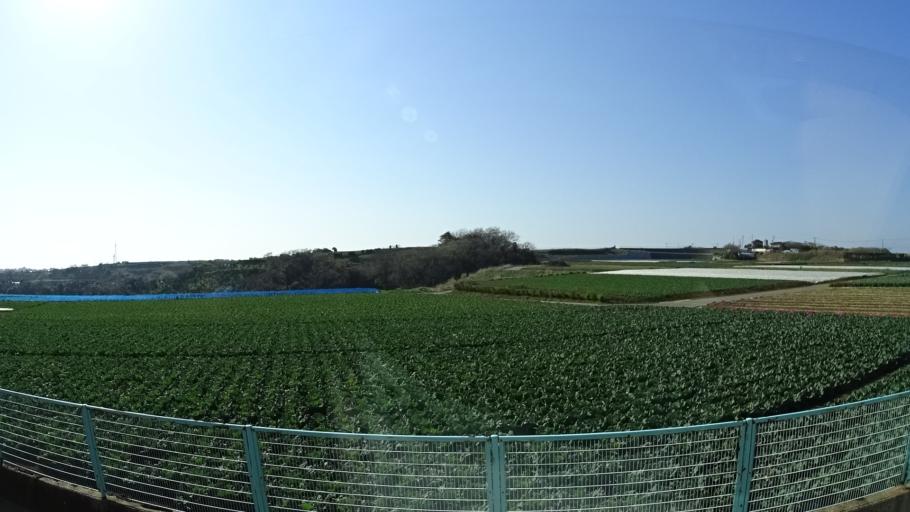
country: JP
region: Kanagawa
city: Miura
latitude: 35.1538
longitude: 139.6461
